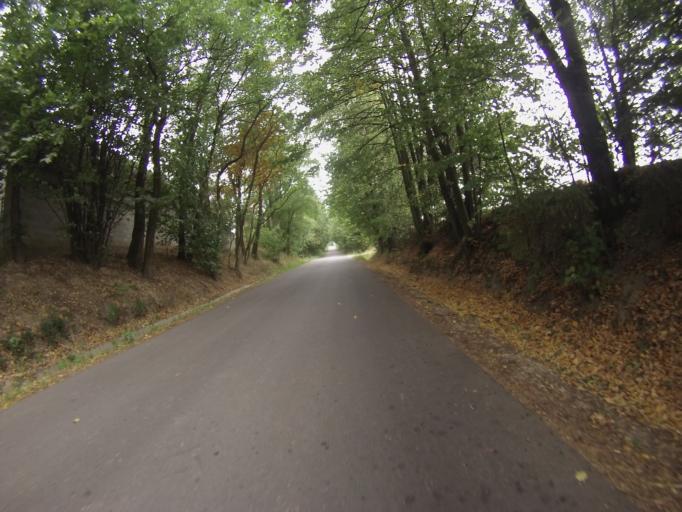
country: PL
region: Swietokrzyskie
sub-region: Powiat kielecki
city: Lagow
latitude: 50.7414
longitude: 21.0517
